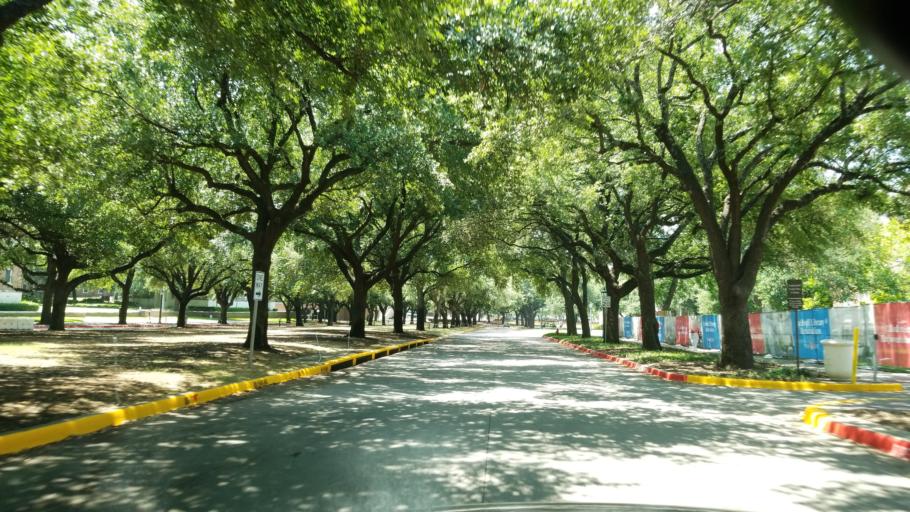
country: US
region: Texas
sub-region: Dallas County
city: Highland Park
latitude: 32.8406
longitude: -96.7852
